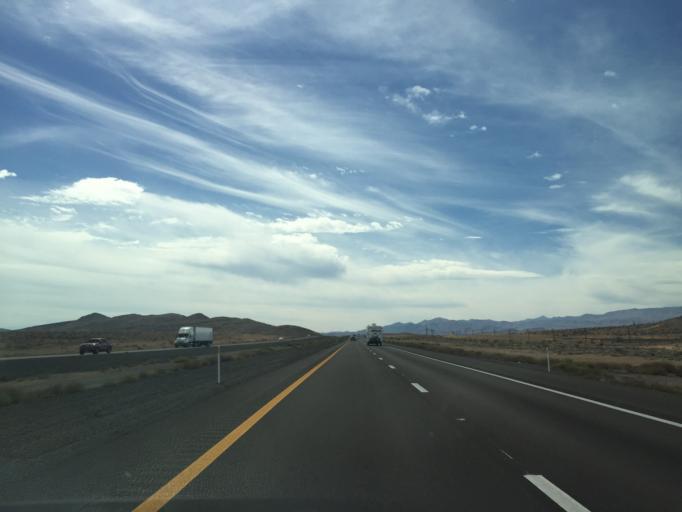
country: US
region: Nevada
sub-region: Clark County
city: Moapa Town
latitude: 36.4801
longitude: -114.8056
